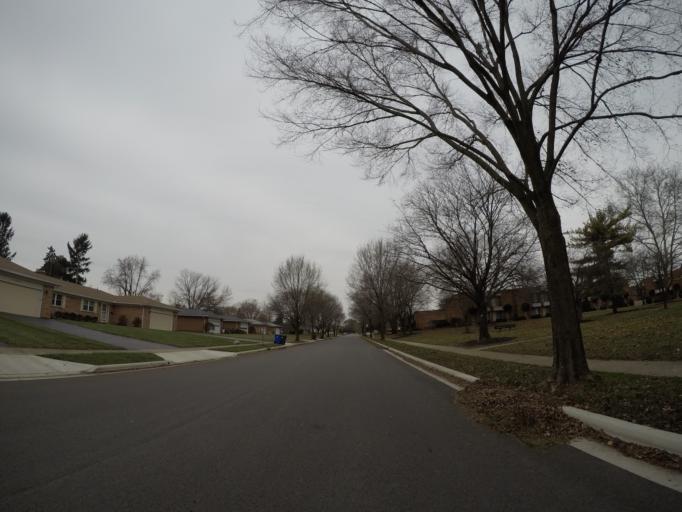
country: US
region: Ohio
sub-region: Franklin County
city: Upper Arlington
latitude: 40.0523
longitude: -83.0724
